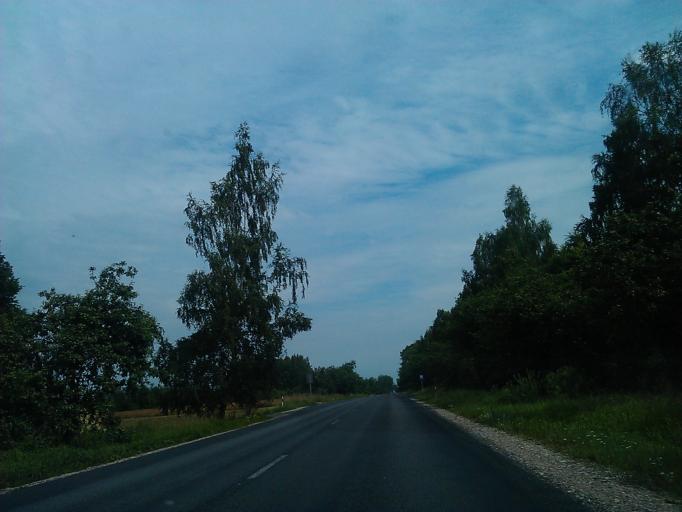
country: LV
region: Priekuli
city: Priekuli
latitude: 57.3791
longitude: 25.4005
